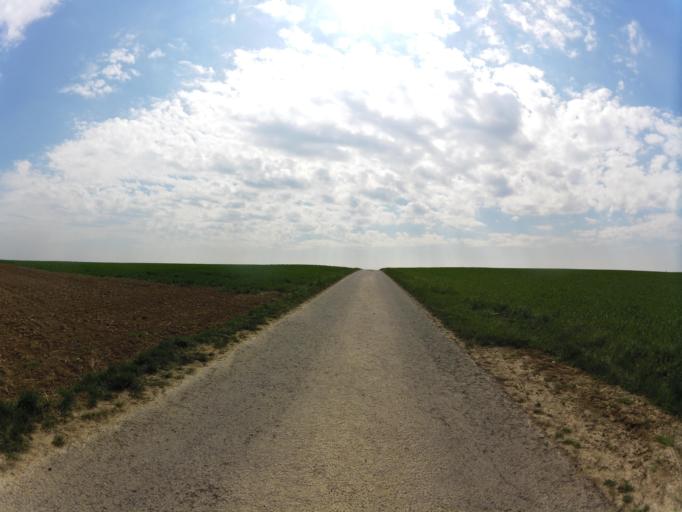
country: DE
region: Bavaria
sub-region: Regierungsbezirk Unterfranken
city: Winterhausen
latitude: 49.6911
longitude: 10.0045
